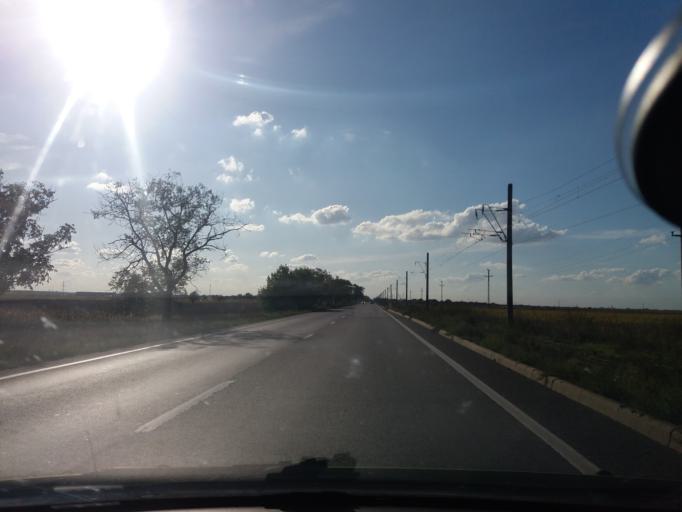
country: RO
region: Arad
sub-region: Comuna Paulis
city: Sambateni
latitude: 46.1453
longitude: 21.5032
